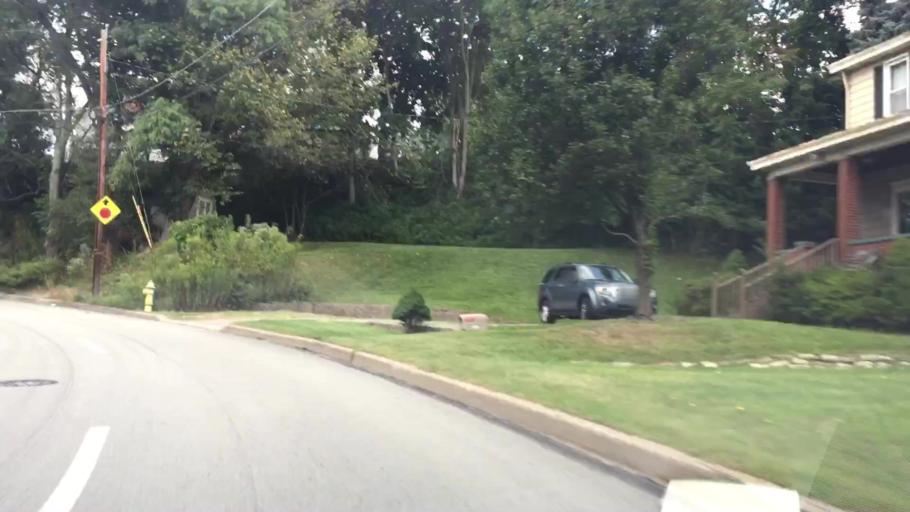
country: US
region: Pennsylvania
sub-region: Allegheny County
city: Millvale
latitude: 40.4945
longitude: -80.0072
